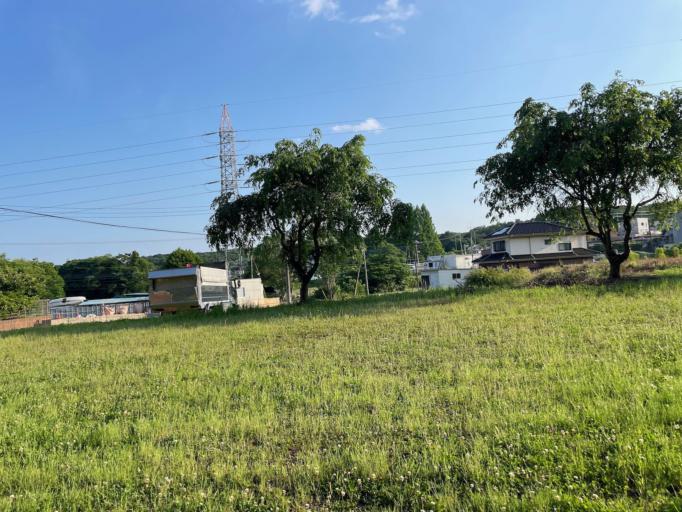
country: JP
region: Saitama
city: Sakado
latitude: 36.0034
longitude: 139.3779
